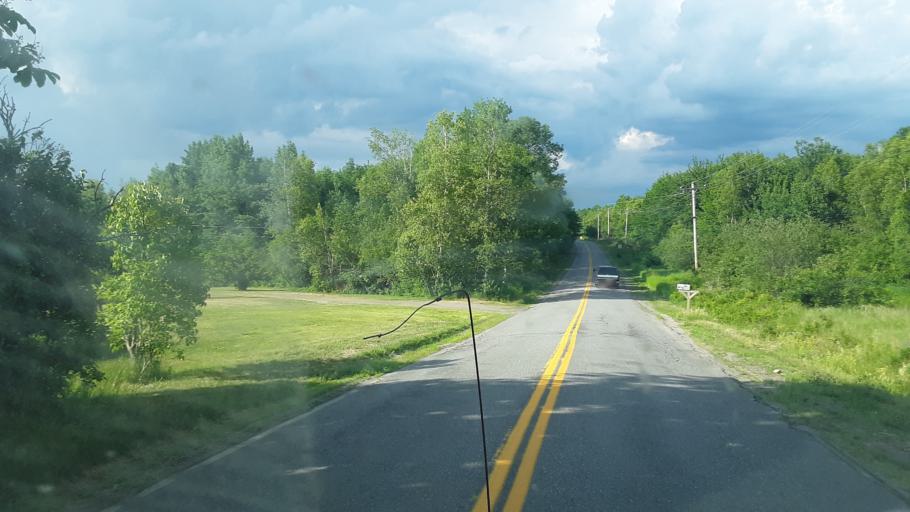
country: US
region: Maine
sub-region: Washington County
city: Calais
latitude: 45.1024
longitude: -67.5108
